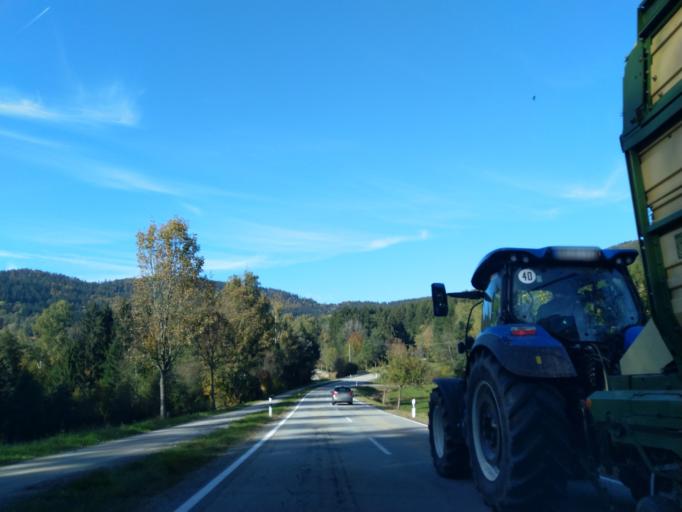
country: DE
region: Bavaria
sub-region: Lower Bavaria
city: Bernried
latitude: 48.9186
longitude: 12.9229
